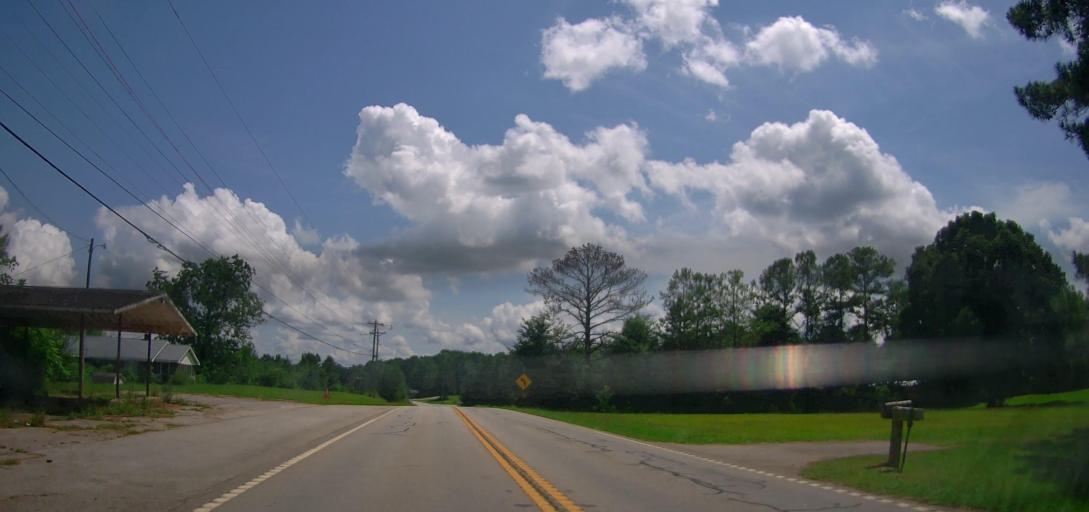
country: US
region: Georgia
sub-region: Carroll County
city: Bowdon
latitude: 33.3951
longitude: -85.2531
